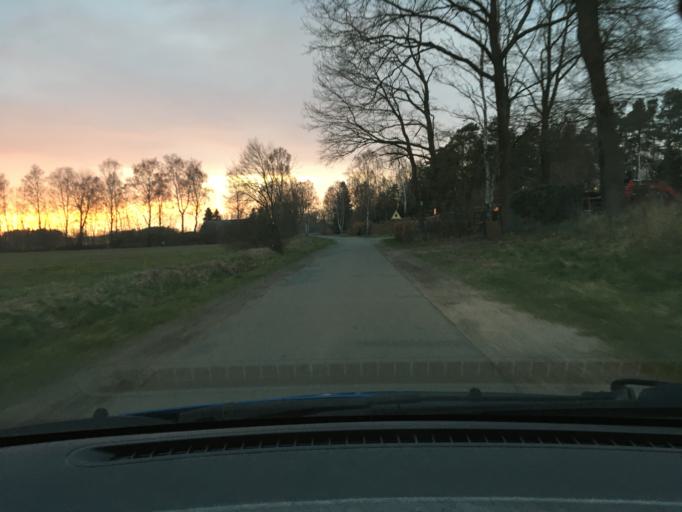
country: DE
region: Lower Saxony
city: Bleckede
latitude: 53.2967
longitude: 10.6802
